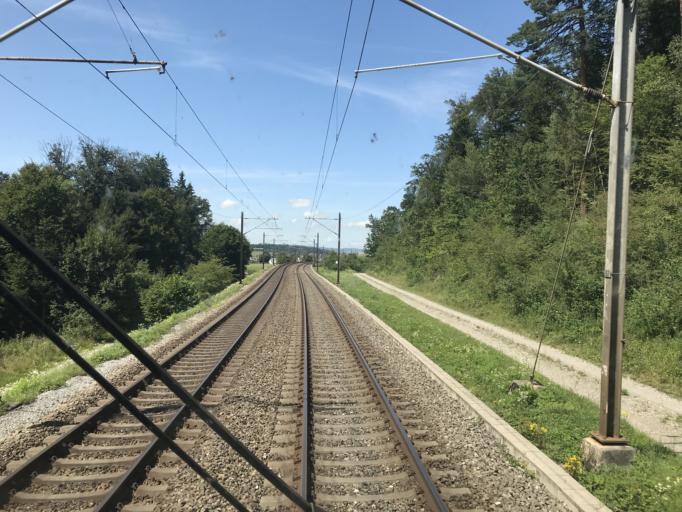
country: CH
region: Zurich
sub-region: Bezirk Uster
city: Wangen
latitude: 47.4261
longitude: 8.6517
